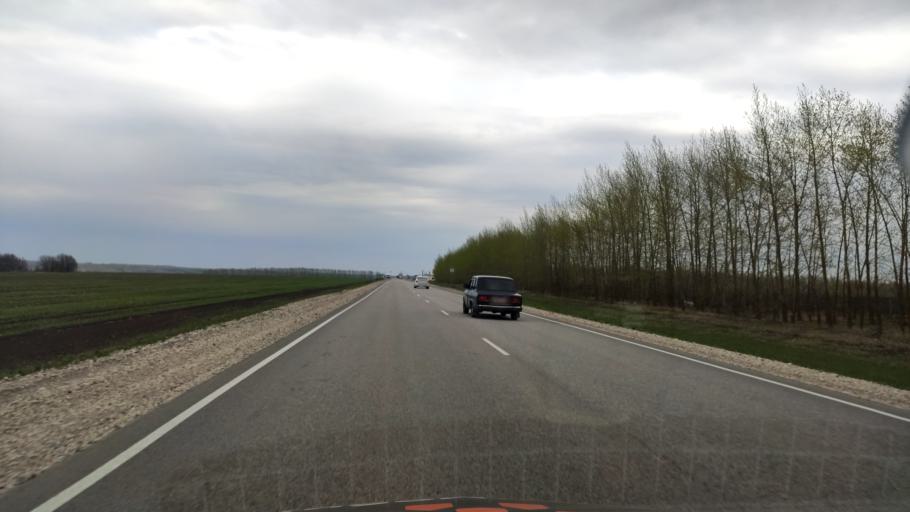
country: RU
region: Voronezj
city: Nizhnedevitsk
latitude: 51.5846
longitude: 38.5315
